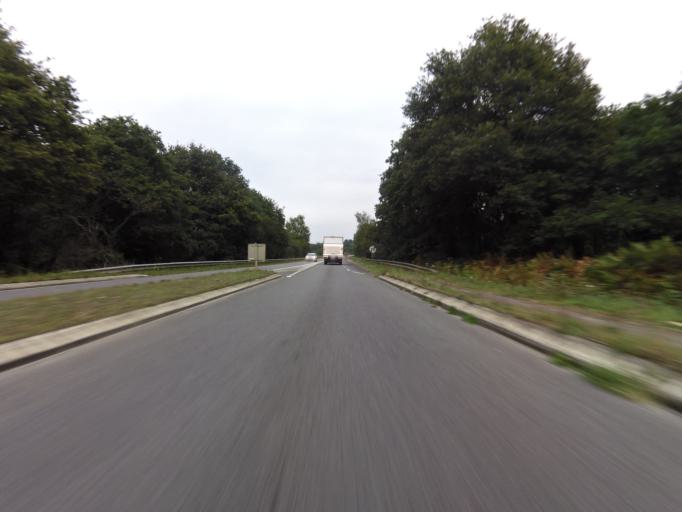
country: FR
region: Brittany
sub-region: Departement du Morbihan
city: Saint-Ave
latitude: 47.6864
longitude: -2.7616
